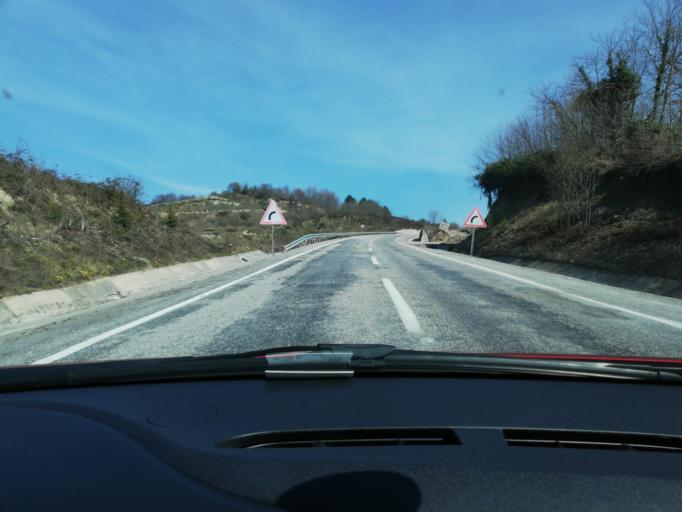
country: TR
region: Bartin
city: Amasra
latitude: 41.7274
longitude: 32.4058
